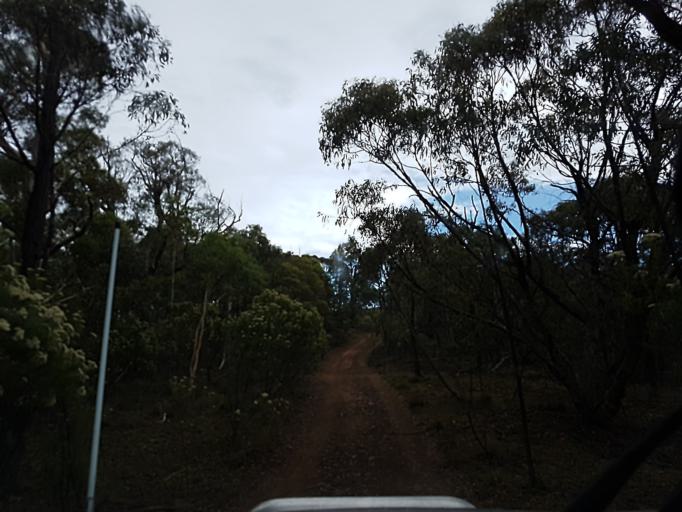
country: AU
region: New South Wales
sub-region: Snowy River
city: Jindabyne
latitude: -36.9100
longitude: 148.3376
